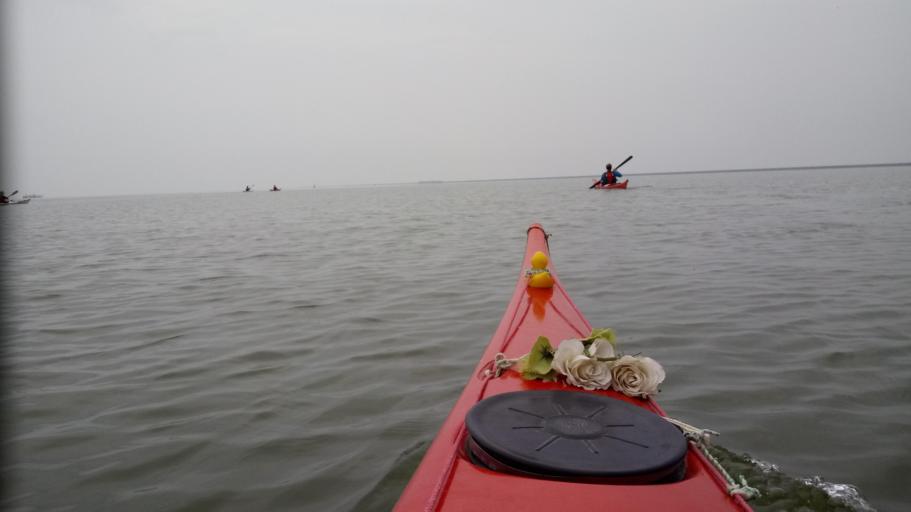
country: NL
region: Flevoland
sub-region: Gemeente Lelystad
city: Lelystad
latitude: 52.5877
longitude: 5.4174
